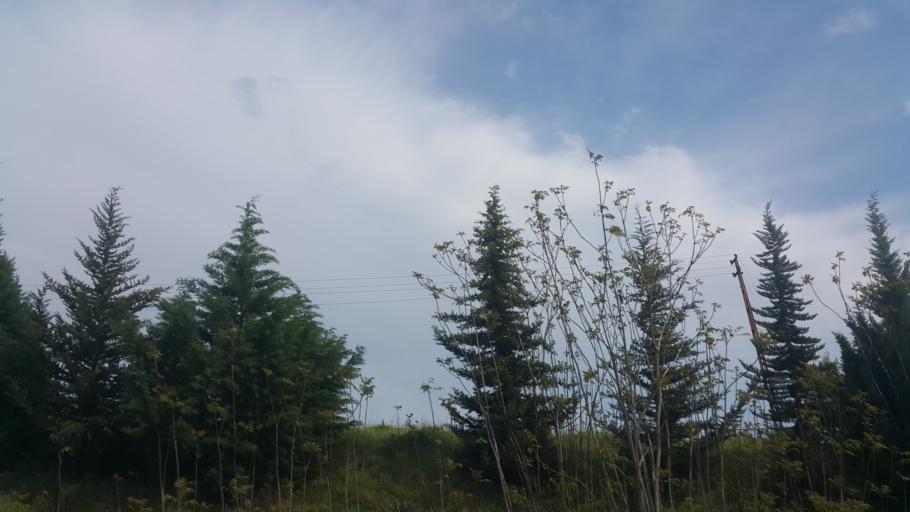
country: TR
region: Mersin
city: Kazanli
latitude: 36.9394
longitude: 34.7208
